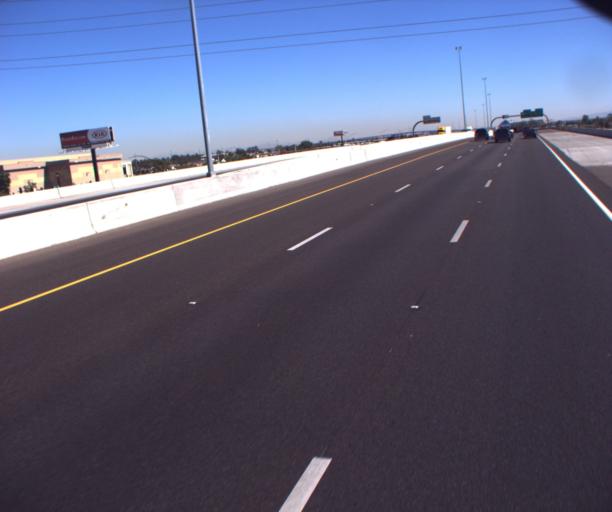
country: US
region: Arizona
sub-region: Maricopa County
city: Citrus Park
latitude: 33.4620
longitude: -112.4626
